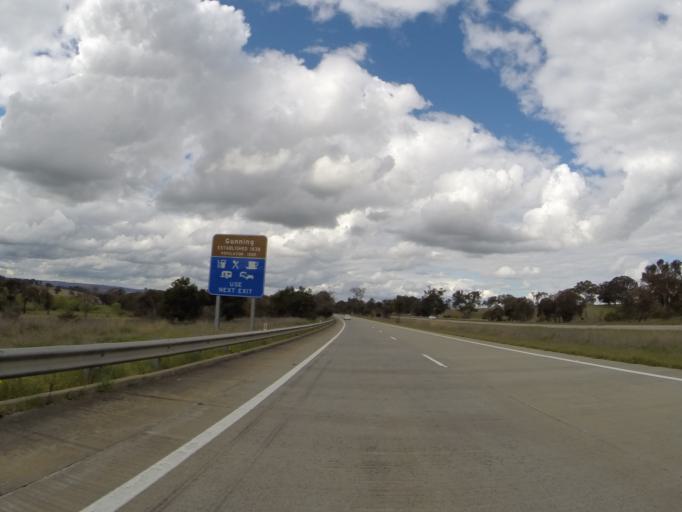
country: AU
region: New South Wales
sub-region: Yass Valley
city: Gundaroo
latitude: -34.7890
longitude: 149.2310
